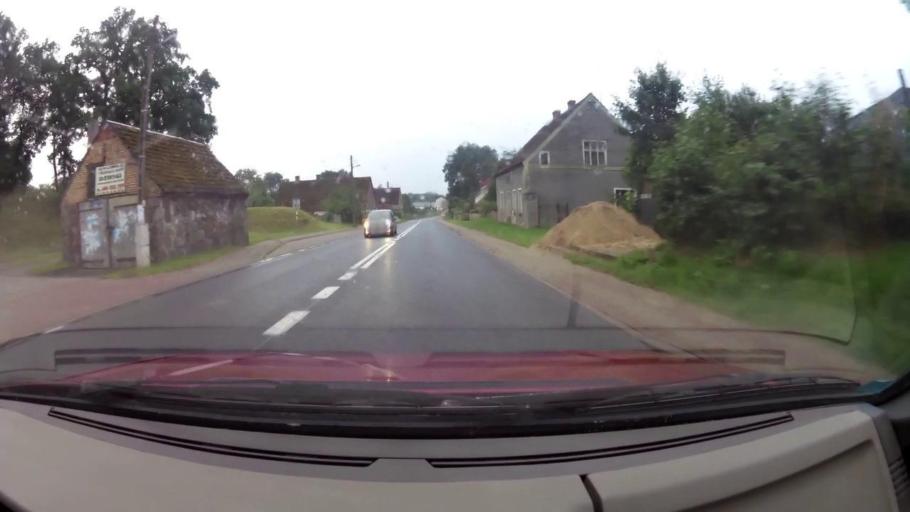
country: PL
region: West Pomeranian Voivodeship
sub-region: Powiat stargardzki
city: Stara Dabrowa
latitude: 53.3835
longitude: 15.1750
